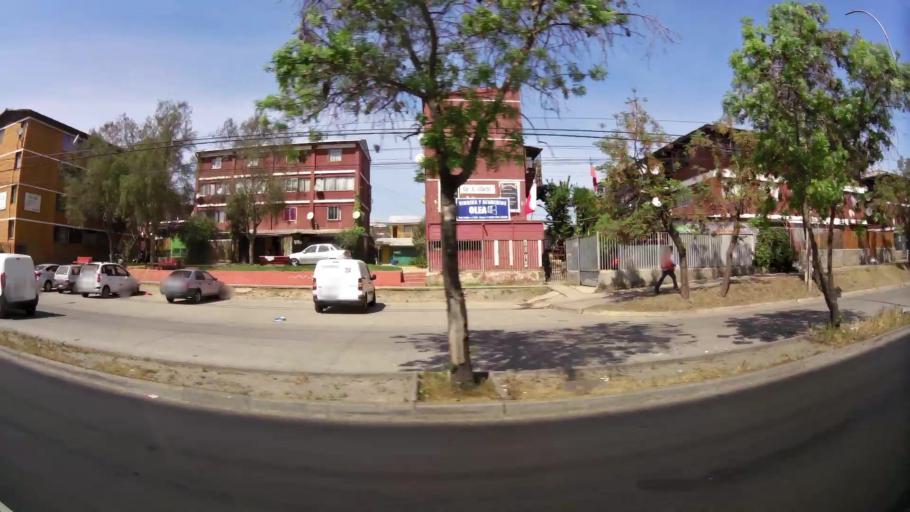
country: CL
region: Santiago Metropolitan
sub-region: Provincia de Santiago
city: Lo Prado
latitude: -33.4448
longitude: -70.7454
